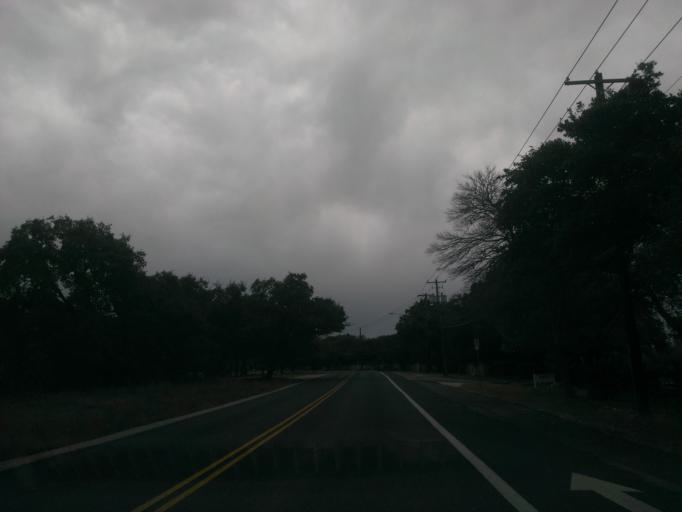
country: US
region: Texas
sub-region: Williamson County
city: Jollyville
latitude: 30.3792
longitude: -97.7652
